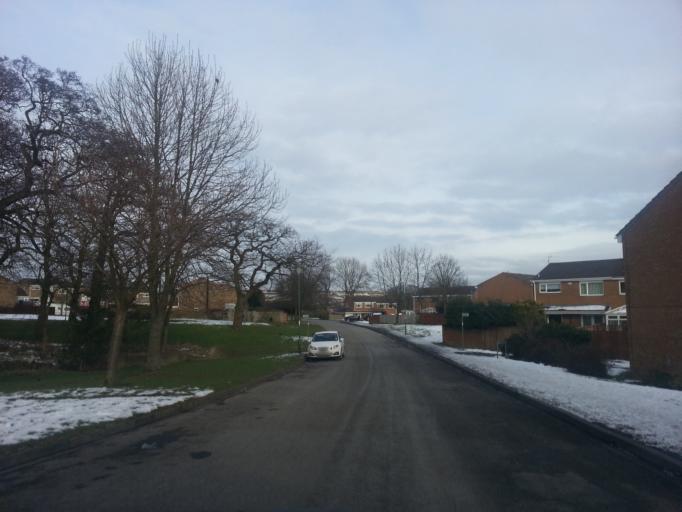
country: GB
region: England
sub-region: County Durham
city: Crook
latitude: 54.7094
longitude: -1.7588
